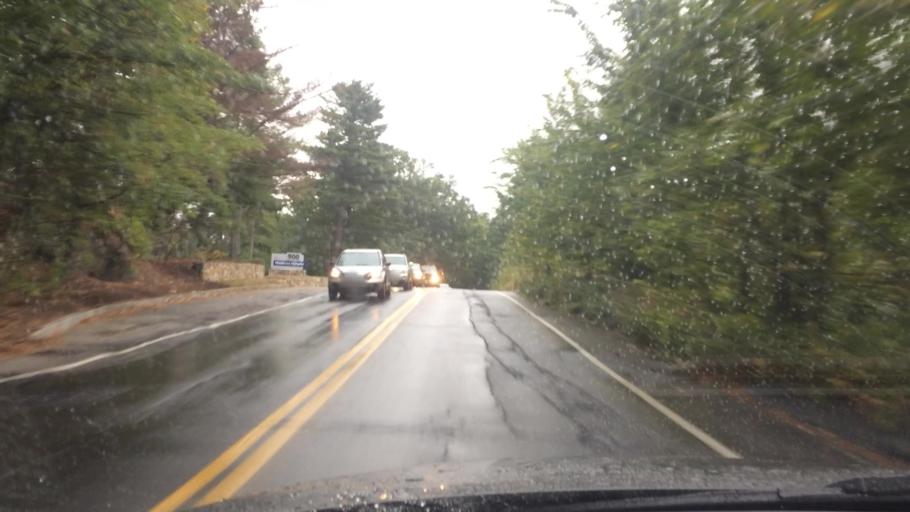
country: US
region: Massachusetts
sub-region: Middlesex County
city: Pinehurst
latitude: 42.5250
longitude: -71.2536
